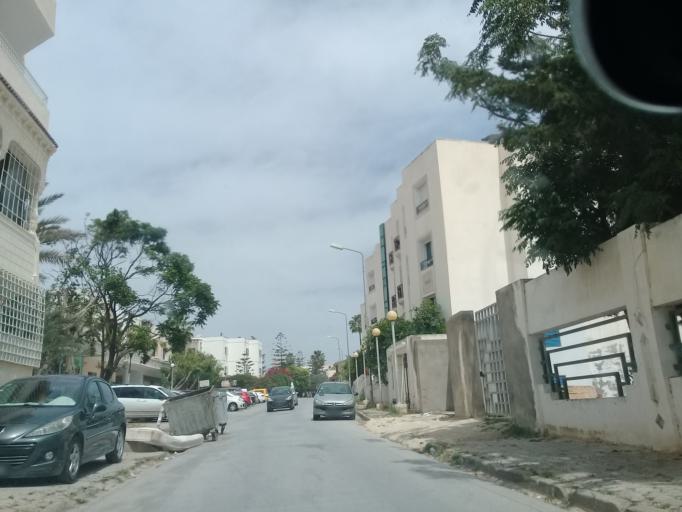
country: TN
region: Tunis
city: Tunis
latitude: 36.8400
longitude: 10.1594
